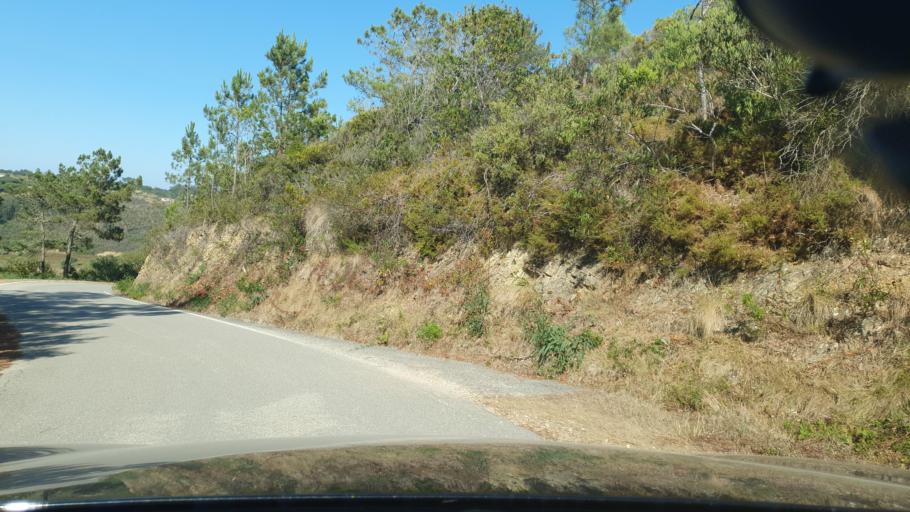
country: PT
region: Faro
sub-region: Aljezur
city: Aljezur
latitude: 37.4344
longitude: -8.7932
